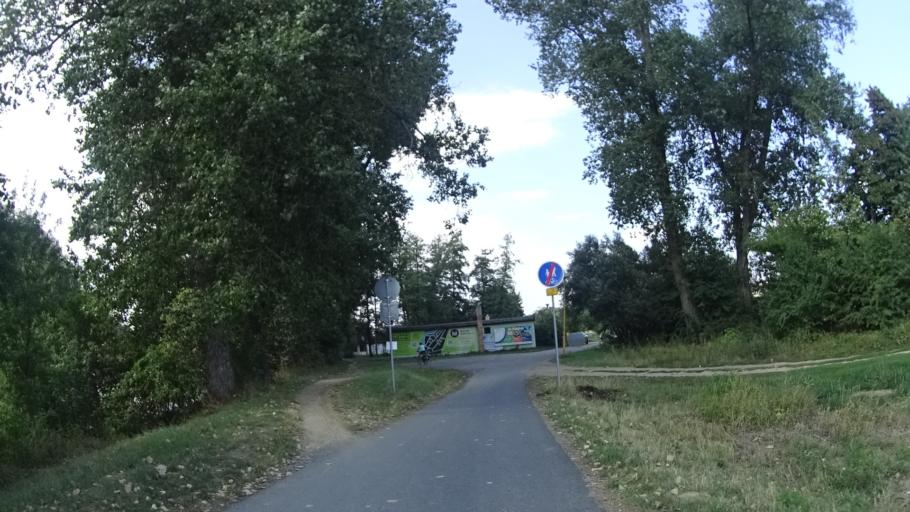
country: CZ
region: Zlin
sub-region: Okres Zlin
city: Napajedla
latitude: 49.1562
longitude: 17.5087
